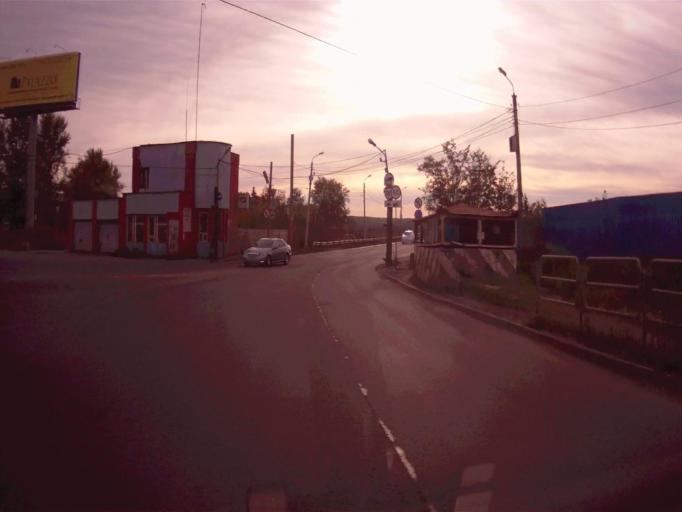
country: RU
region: Chelyabinsk
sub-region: Gorod Chelyabinsk
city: Chelyabinsk
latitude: 55.1481
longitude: 61.3031
